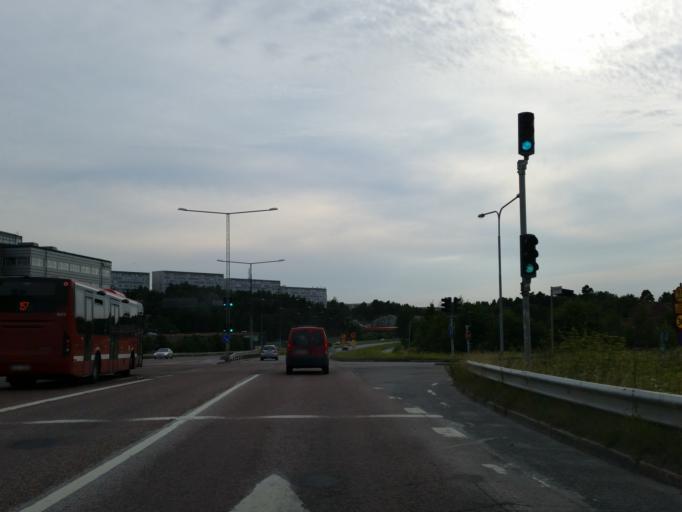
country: SE
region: Stockholm
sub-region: Solna Kommun
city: Rasunda
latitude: 59.3808
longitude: 17.9703
